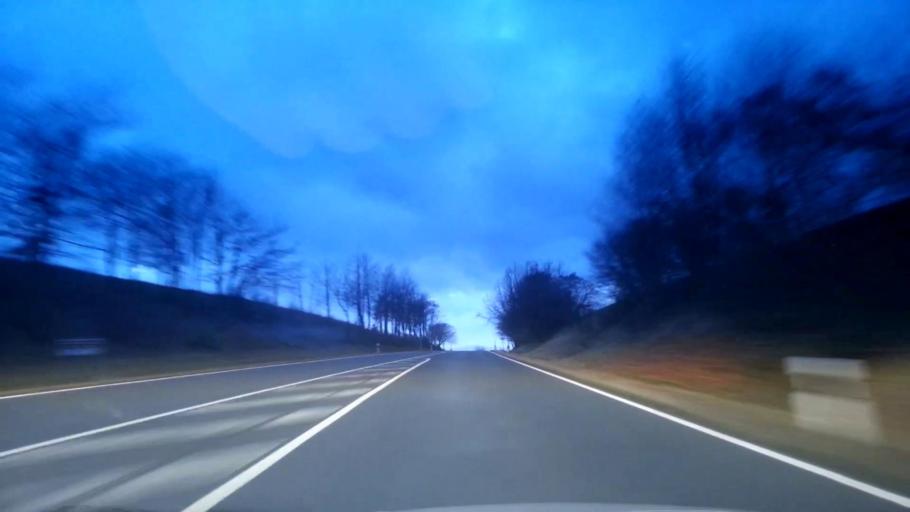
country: DE
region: Bavaria
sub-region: Upper Palatinate
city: Fuchsmuhl
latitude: 49.9405
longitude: 12.1199
